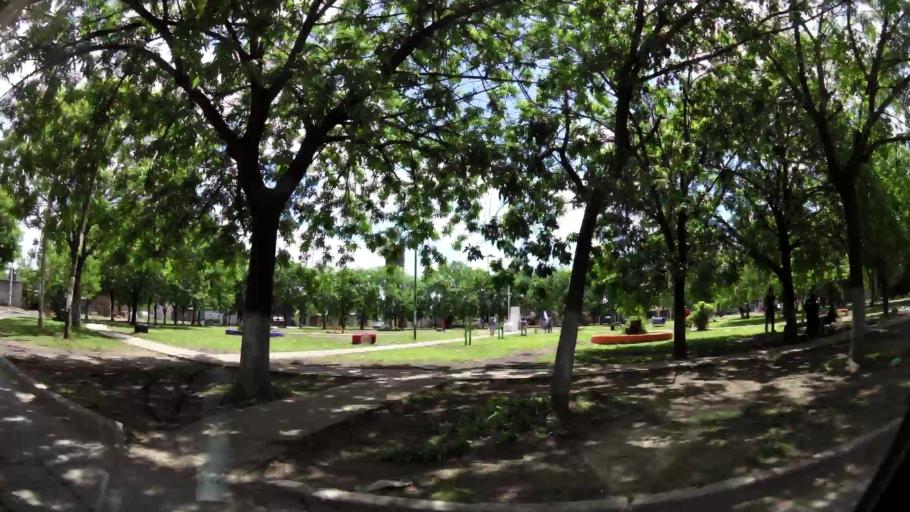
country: AR
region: Buenos Aires
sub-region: Partido de Quilmes
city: Quilmes
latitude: -34.8256
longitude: -58.2329
